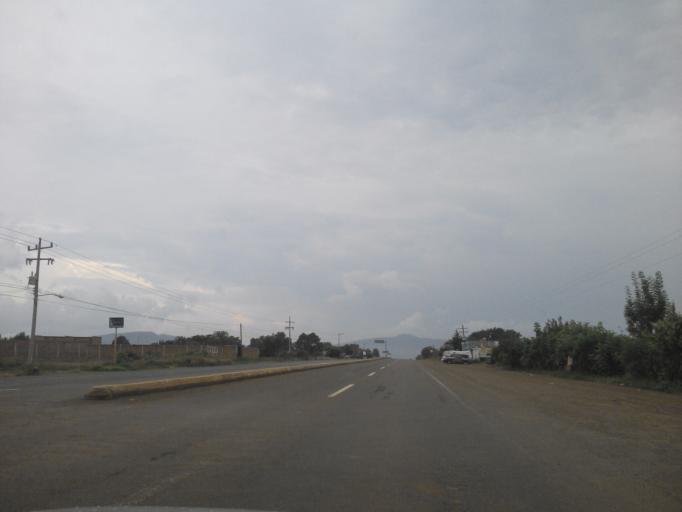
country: MX
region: Jalisco
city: San Jose de Gracia
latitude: 20.7314
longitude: -102.4881
